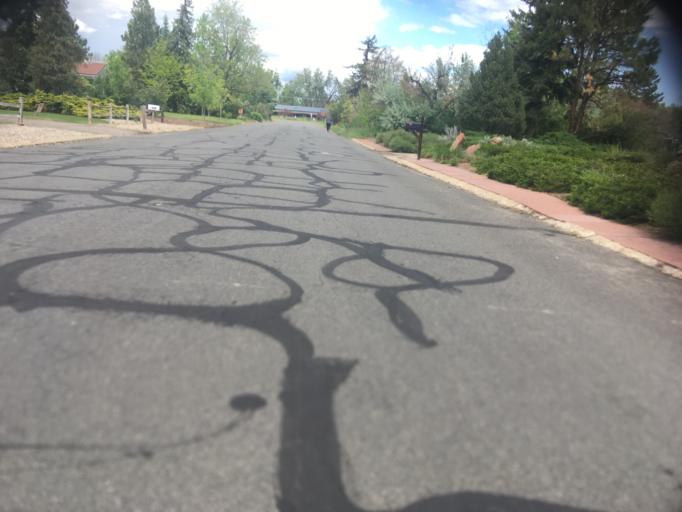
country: US
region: Colorado
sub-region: Boulder County
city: Boulder
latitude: 40.0052
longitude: -105.2328
